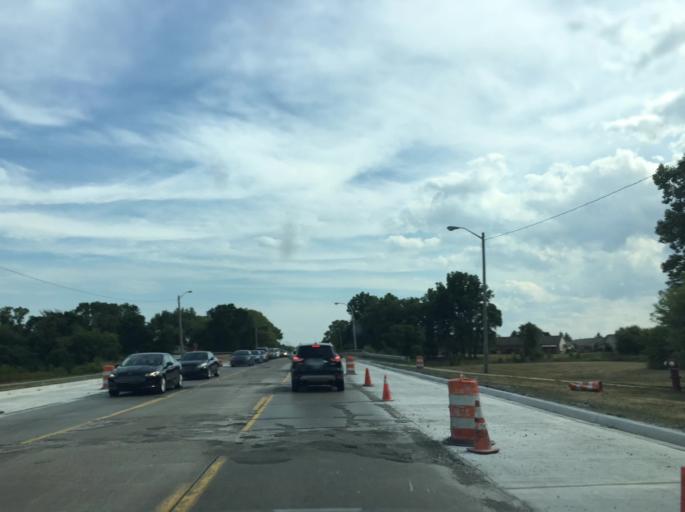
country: US
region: Michigan
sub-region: Macomb County
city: Fraser
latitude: 42.5508
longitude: -82.9897
